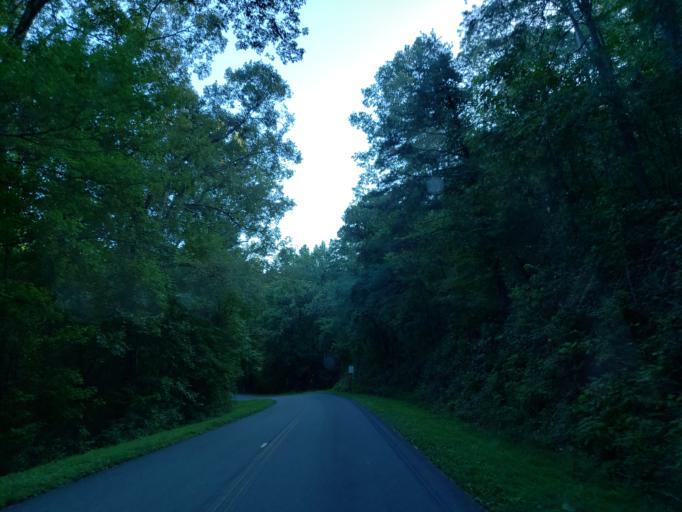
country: US
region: Georgia
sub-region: Bartow County
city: Rydal
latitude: 34.4117
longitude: -84.6878
